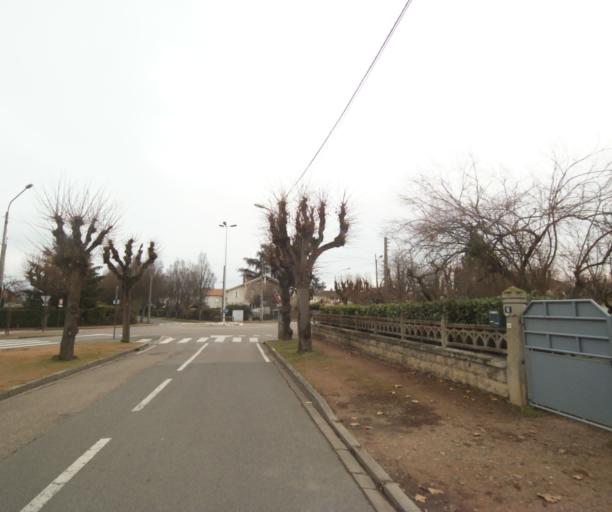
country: FR
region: Rhone-Alpes
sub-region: Departement de la Loire
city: Mably
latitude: 46.0603
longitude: 4.0759
